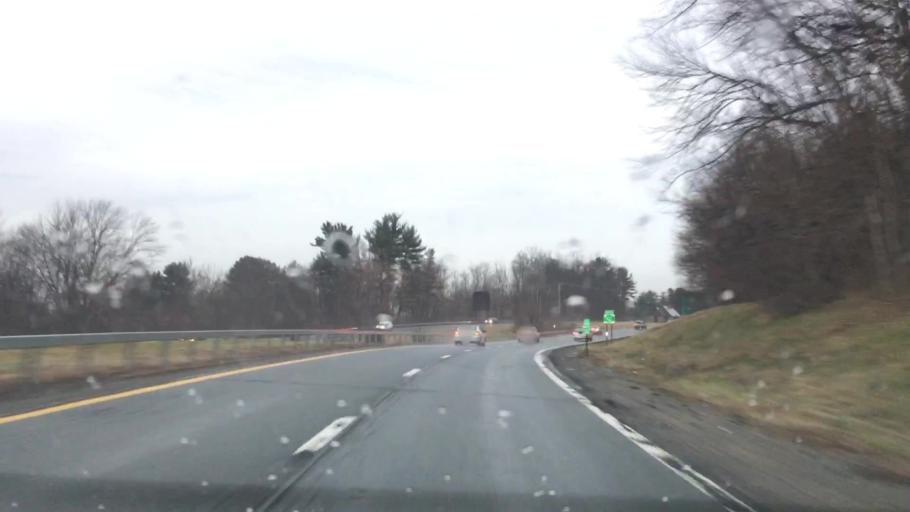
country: US
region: New York
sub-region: Dutchess County
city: Hillside Lake
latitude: 41.5450
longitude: -73.7748
